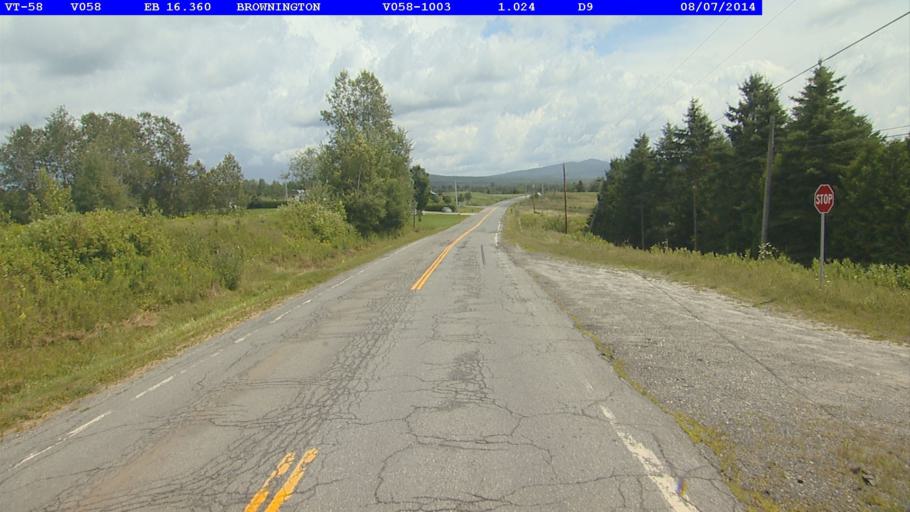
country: US
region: Vermont
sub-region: Orleans County
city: Newport
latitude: 44.8010
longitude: -72.1262
